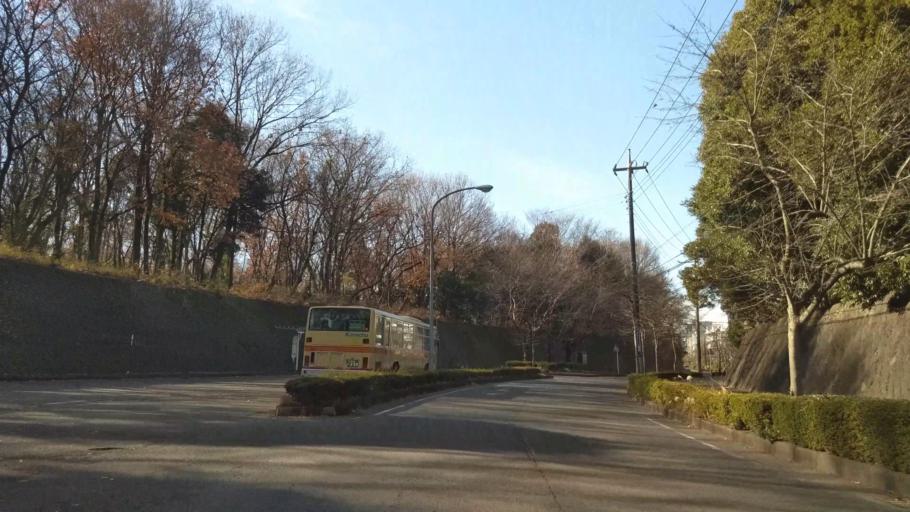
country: JP
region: Kanagawa
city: Hadano
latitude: 35.3522
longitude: 139.2310
